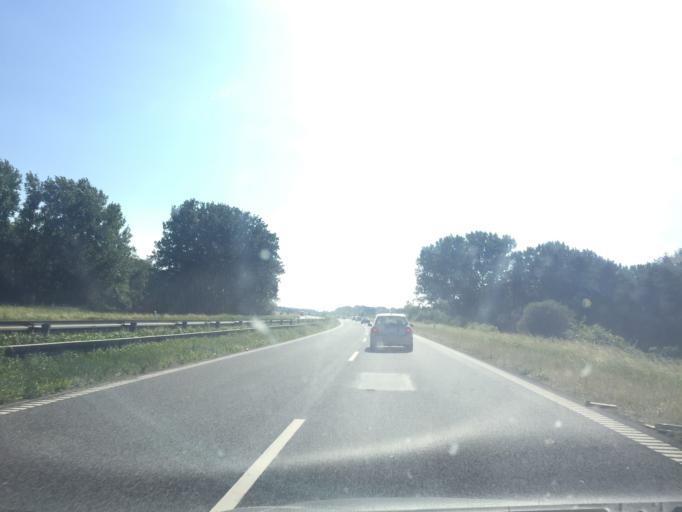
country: DK
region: Zealand
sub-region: Slagelse Kommune
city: Korsor
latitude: 55.3601
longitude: 11.1636
